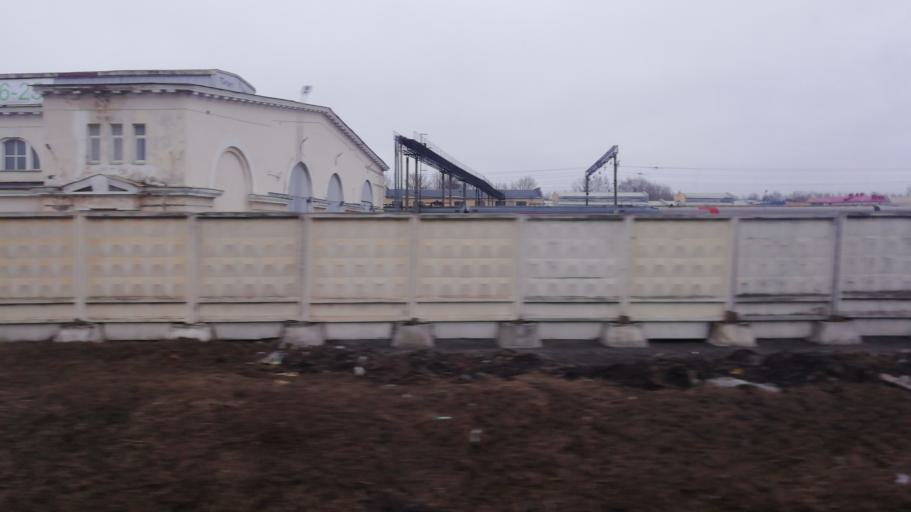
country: RU
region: St.-Petersburg
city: Kupchino
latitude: 59.8858
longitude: 30.3455
